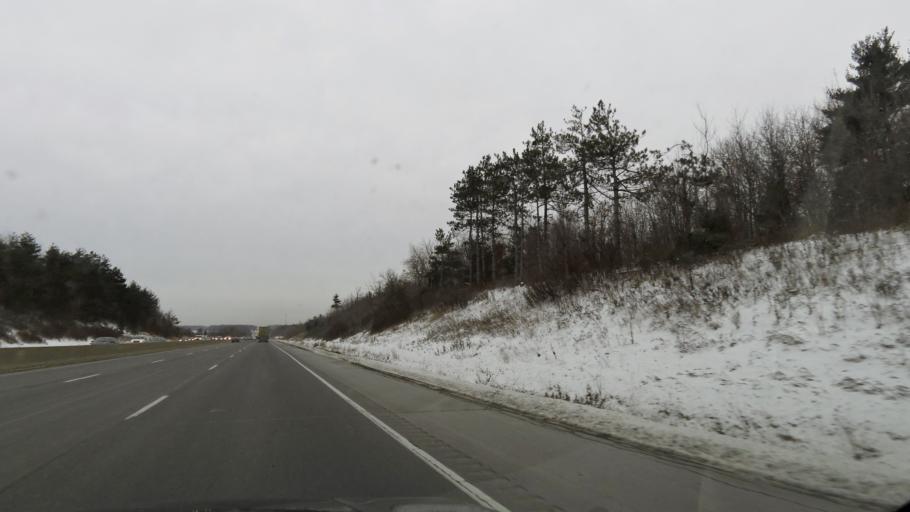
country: CA
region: Ontario
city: Newmarket
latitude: 43.9613
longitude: -79.5759
